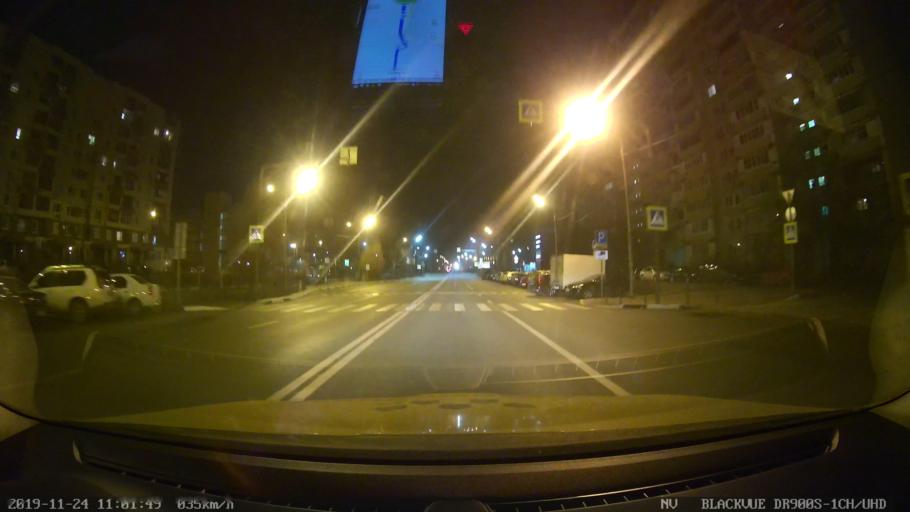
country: RU
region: Moskovskaya
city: Mytishchi
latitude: 55.9068
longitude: 37.7055
